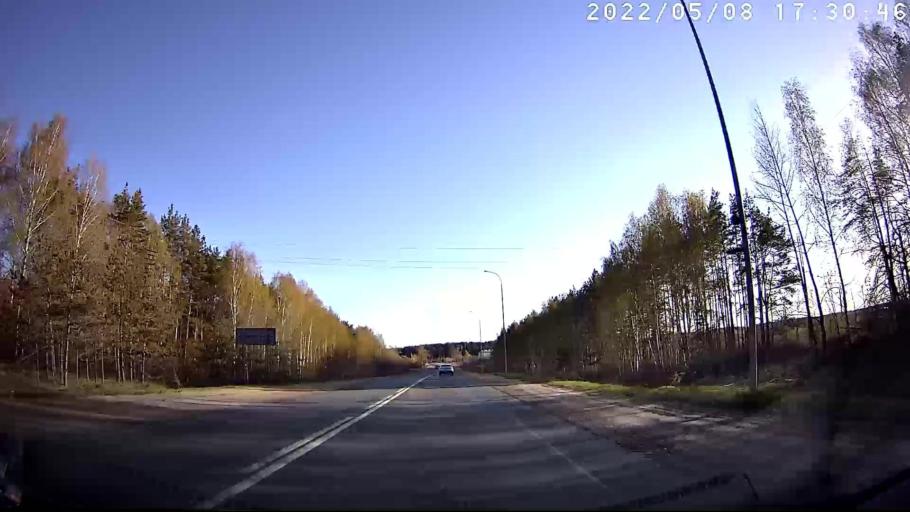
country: RU
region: Mariy-El
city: Volzhsk
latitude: 55.9061
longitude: 48.3596
